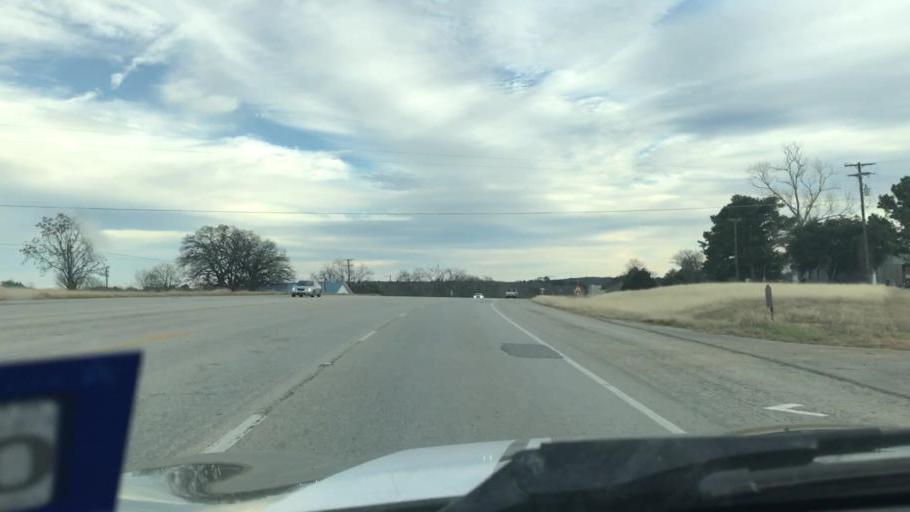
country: US
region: Texas
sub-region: Bastrop County
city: Camp Swift
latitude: 30.2857
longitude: -97.2469
